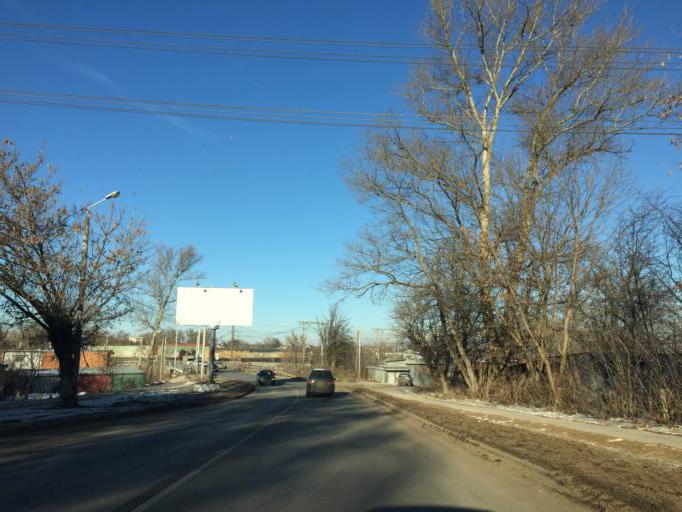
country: RU
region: Tula
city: Tula
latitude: 54.1898
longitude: 37.5712
